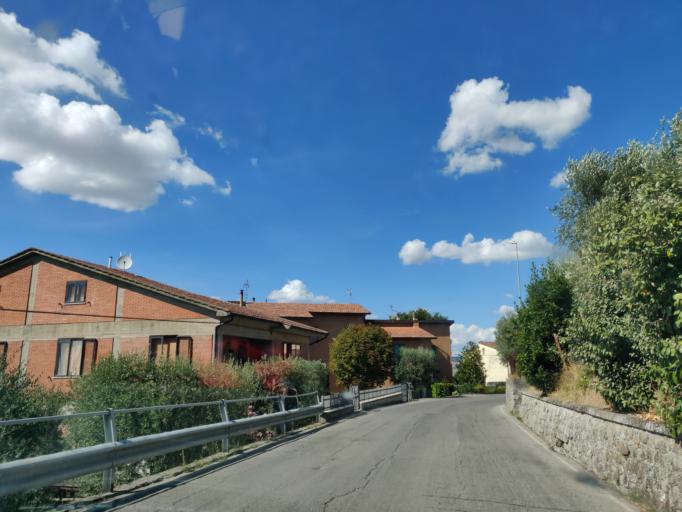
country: IT
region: Tuscany
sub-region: Provincia di Siena
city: Radicofani
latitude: 42.9747
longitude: 11.7387
